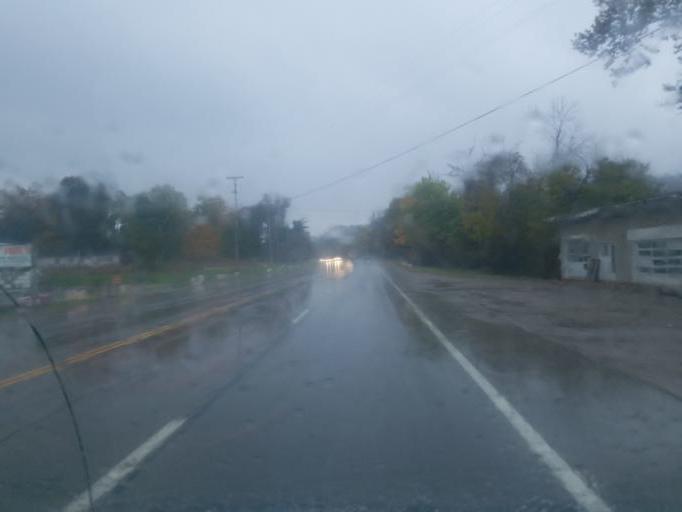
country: US
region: Ohio
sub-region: Muskingum County
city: South Zanesville
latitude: 39.9006
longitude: -82.0002
